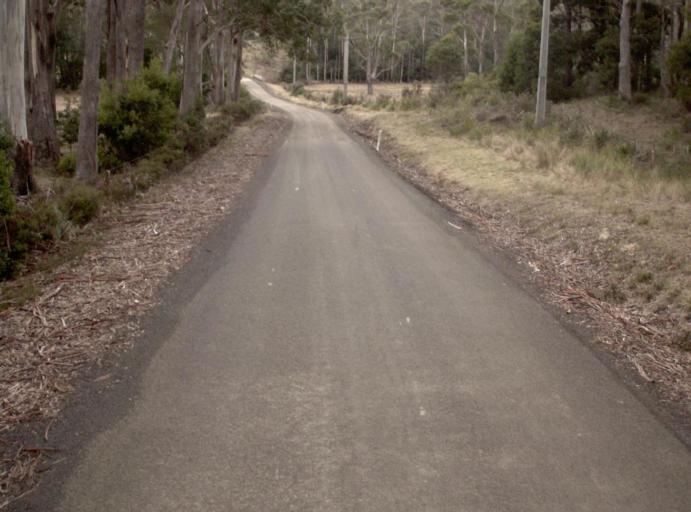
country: AU
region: Tasmania
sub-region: Launceston
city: Newstead
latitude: -41.3433
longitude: 147.3622
